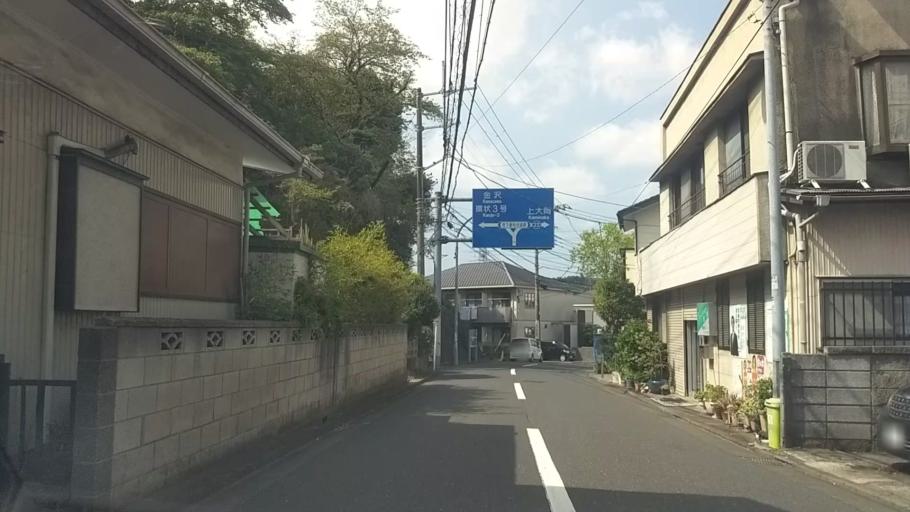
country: JP
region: Kanagawa
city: Yokohama
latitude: 35.3791
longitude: 139.6100
